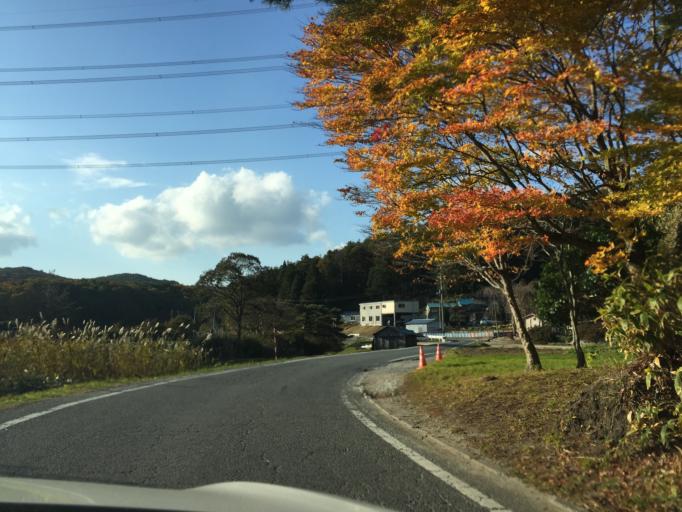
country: JP
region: Fukushima
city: Funehikimachi-funehiki
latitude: 37.2937
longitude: 140.7333
